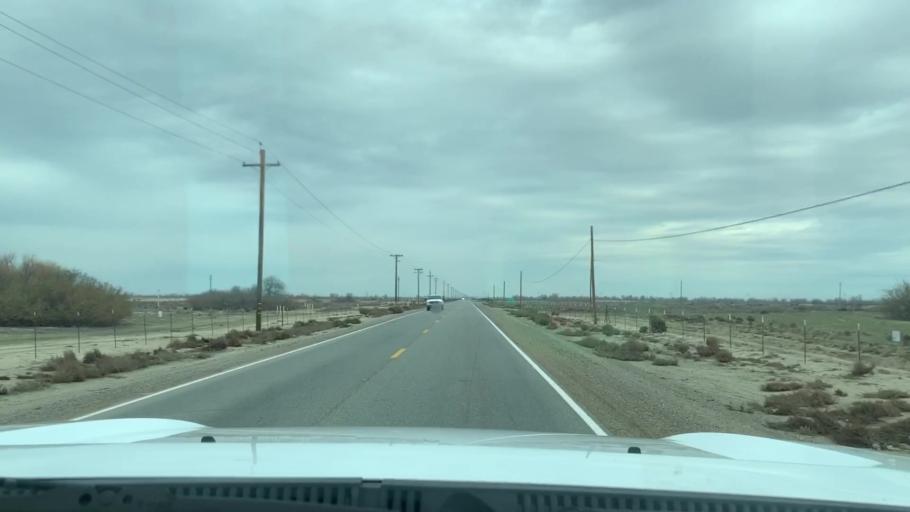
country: US
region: California
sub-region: Kern County
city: Rosedale
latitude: 35.3222
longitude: -119.2524
